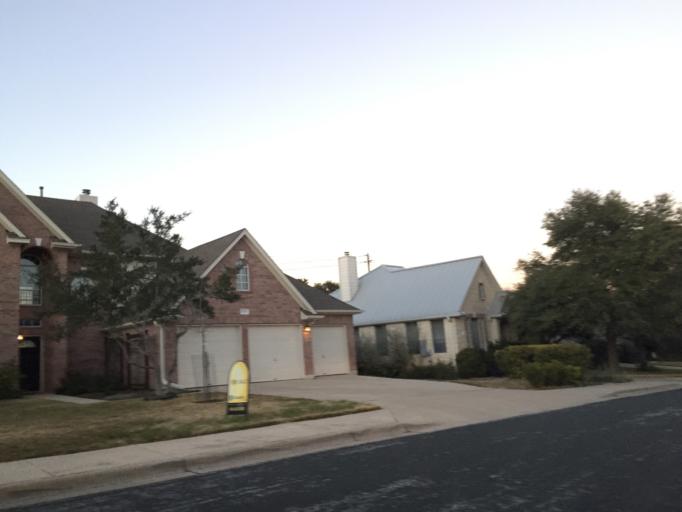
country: US
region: Texas
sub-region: Williamson County
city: Jollyville
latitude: 30.3998
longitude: -97.7668
